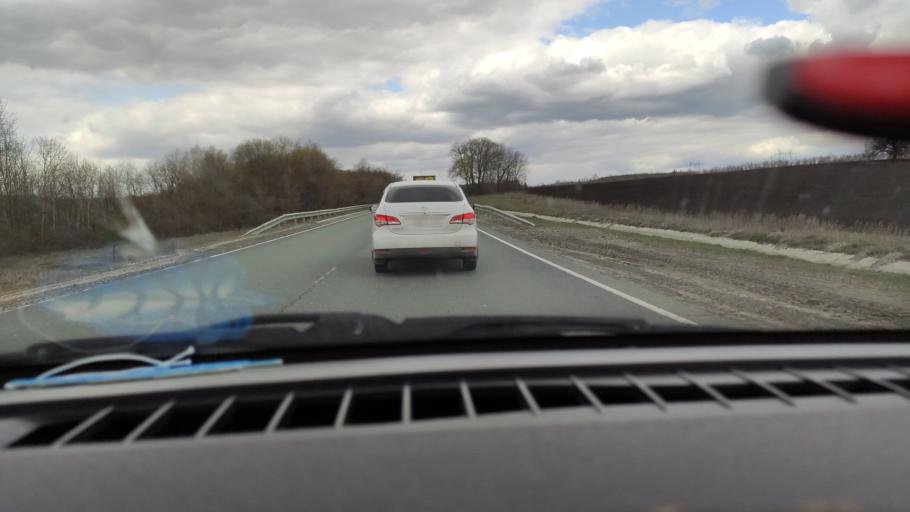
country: RU
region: Saratov
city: Vol'sk
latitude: 52.1036
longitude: 47.4473
